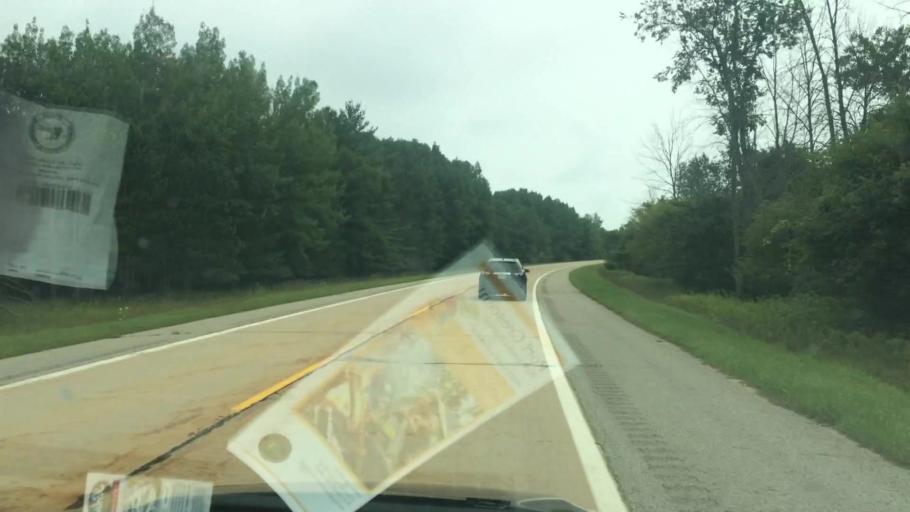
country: US
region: Michigan
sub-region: Huron County
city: Harbor Beach
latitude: 44.0271
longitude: -82.8256
